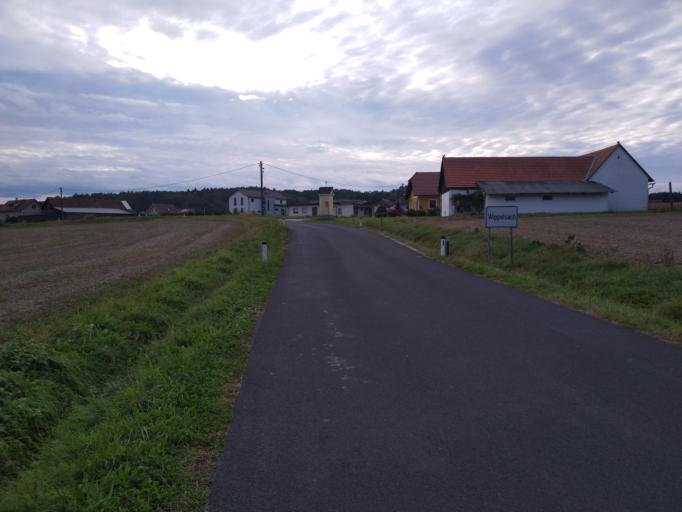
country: AT
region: Styria
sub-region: Politischer Bezirk Leibnitz
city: Grossklein
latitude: 46.7488
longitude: 15.4367
